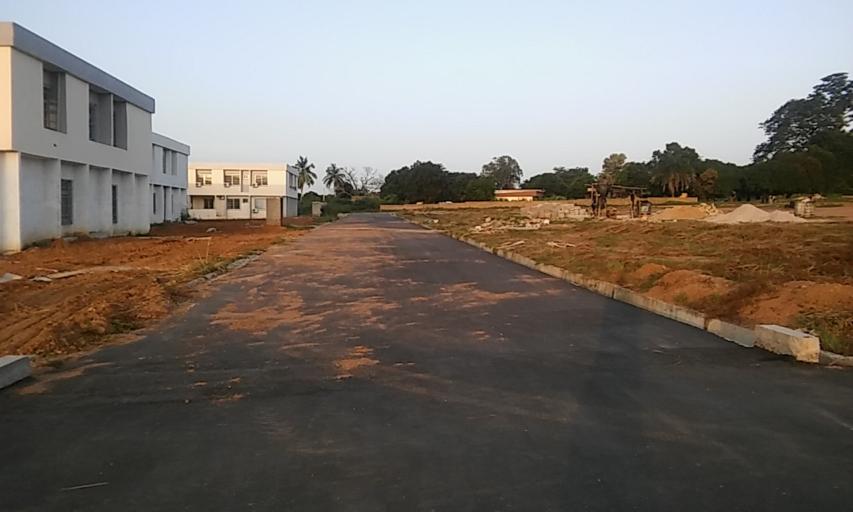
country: CI
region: Vallee du Bandama
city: Bouake
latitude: 7.6904
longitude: -5.0640
